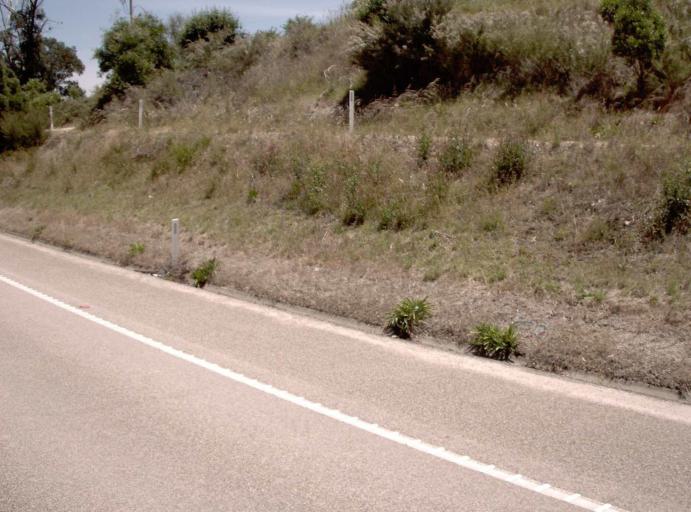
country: AU
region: Victoria
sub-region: East Gippsland
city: Bairnsdale
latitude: -37.7252
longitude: 147.8008
